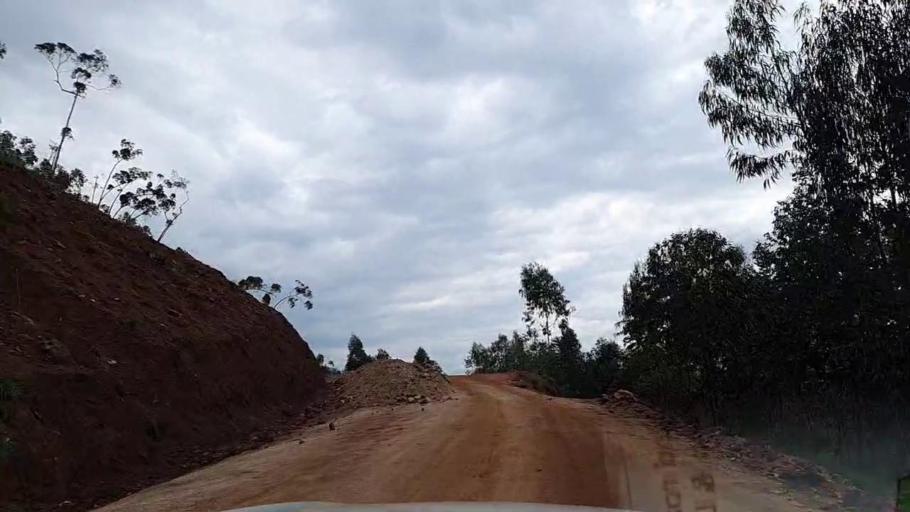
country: RW
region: Southern Province
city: Nzega
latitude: -2.3704
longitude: 29.4499
